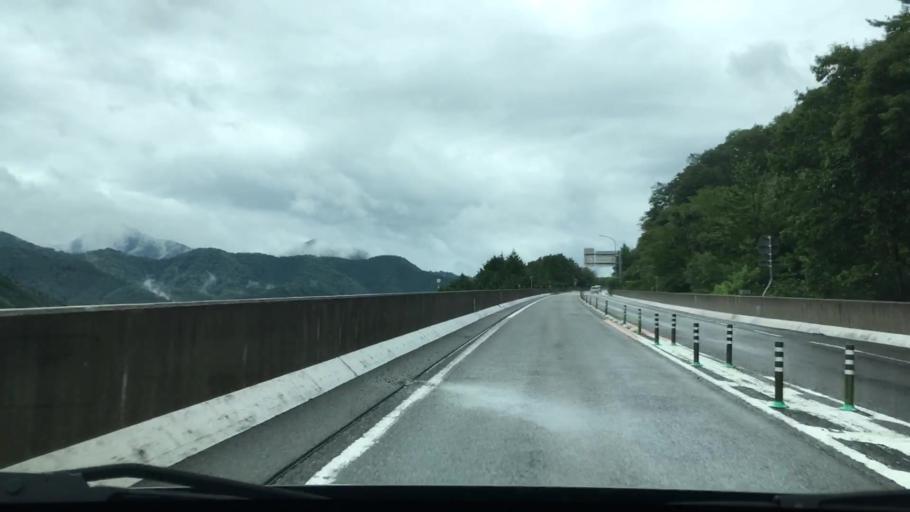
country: JP
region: Hyogo
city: Toyooka
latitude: 35.2840
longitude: 134.8211
